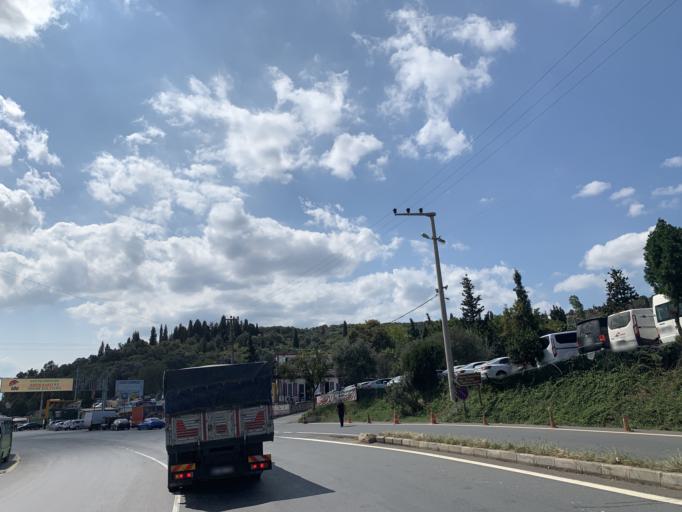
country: TR
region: Kocaeli
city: Darica
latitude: 40.7688
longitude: 29.4244
